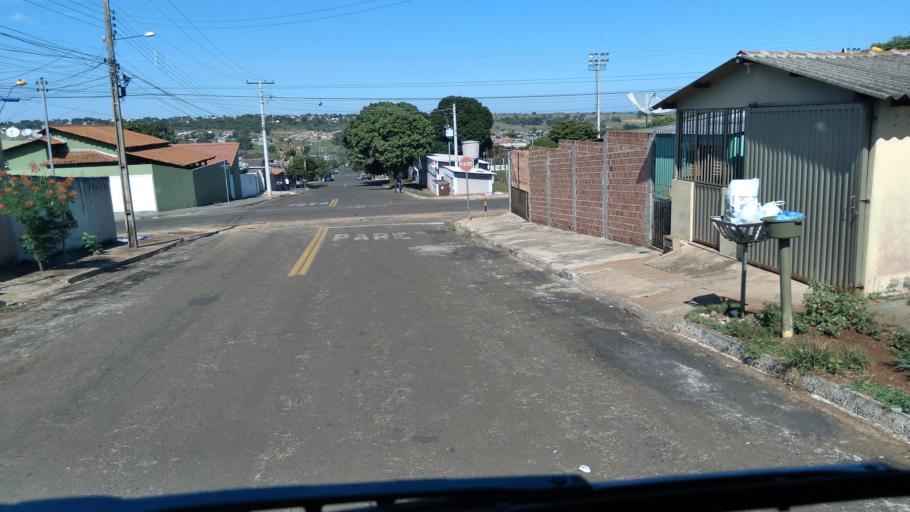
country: BR
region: Goias
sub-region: Mineiros
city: Mineiros
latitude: -17.5710
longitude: -52.5662
